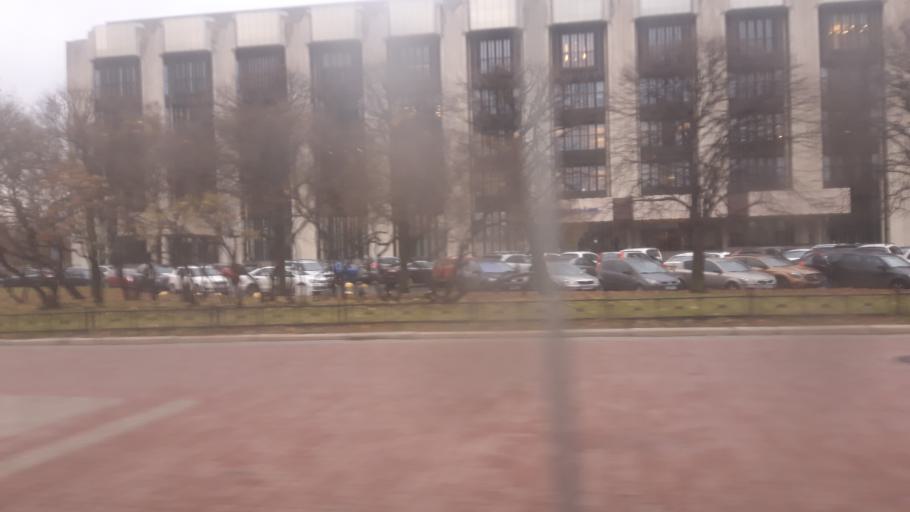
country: RU
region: St.-Petersburg
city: Kupchino
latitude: 59.8434
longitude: 30.3235
